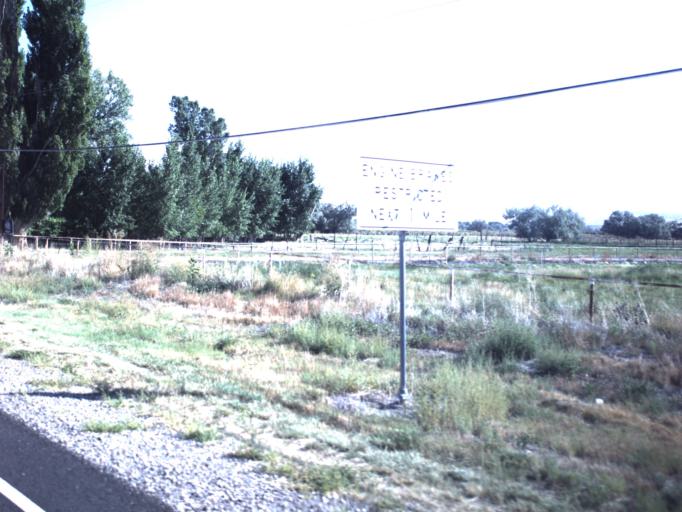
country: US
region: Utah
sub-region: Sevier County
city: Salina
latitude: 38.9960
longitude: -111.8613
